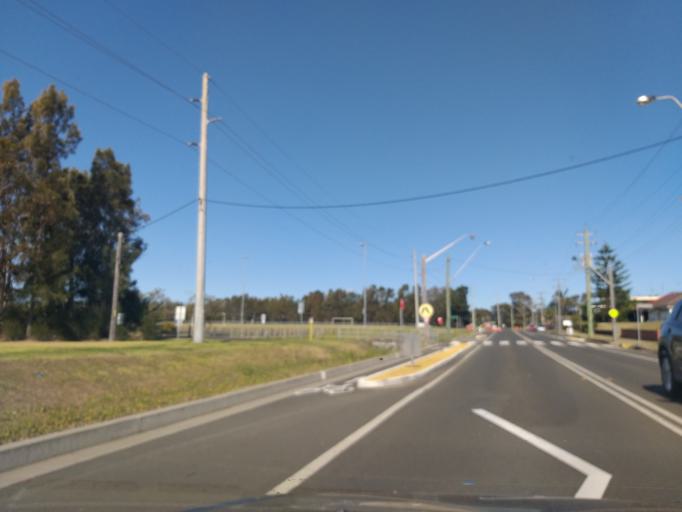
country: AU
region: New South Wales
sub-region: Wollongong
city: Fairy Meadow
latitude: -34.3942
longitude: 150.9013
